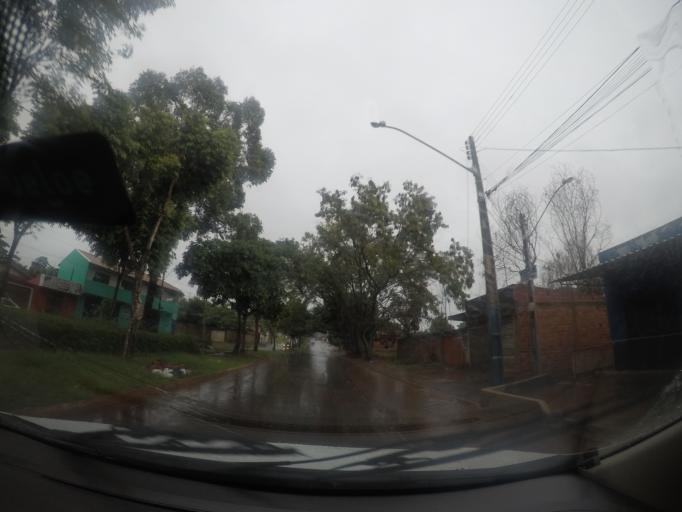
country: BR
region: Goias
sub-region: Goiania
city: Goiania
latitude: -16.6051
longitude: -49.3442
